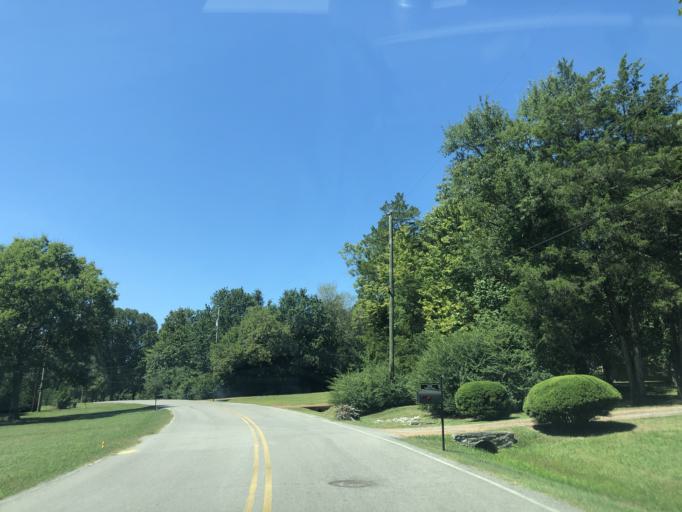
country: US
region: Tennessee
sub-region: Davidson County
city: Forest Hills
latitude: 36.0638
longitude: -86.8380
